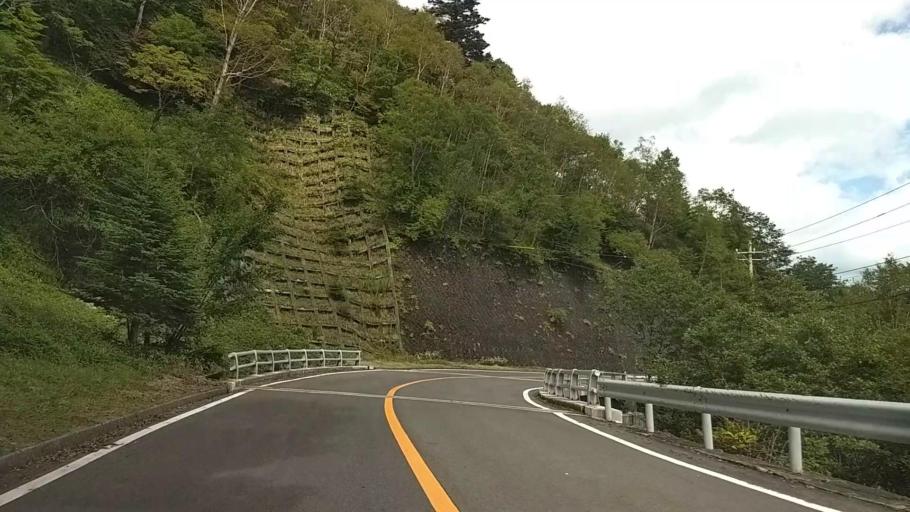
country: JP
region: Tochigi
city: Nikko
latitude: 36.7163
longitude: 139.4888
